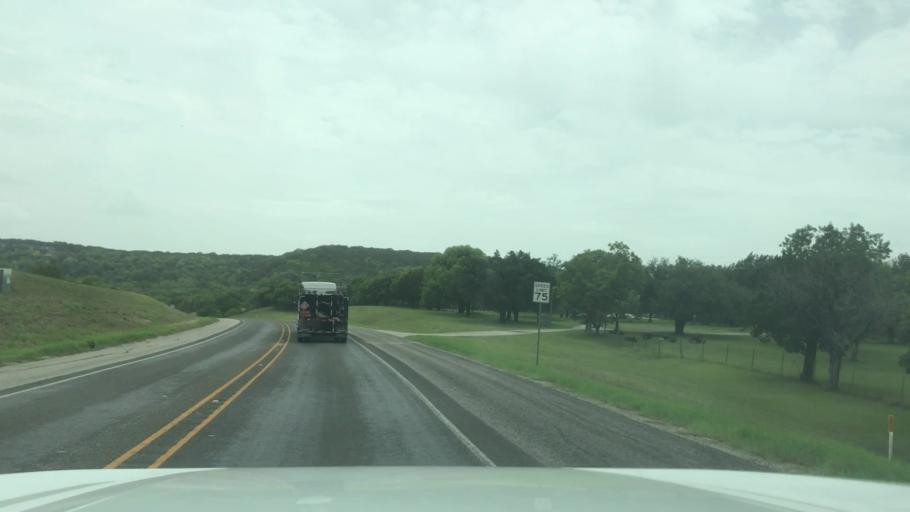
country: US
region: Texas
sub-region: Bosque County
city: Meridian
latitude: 31.9051
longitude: -97.6608
